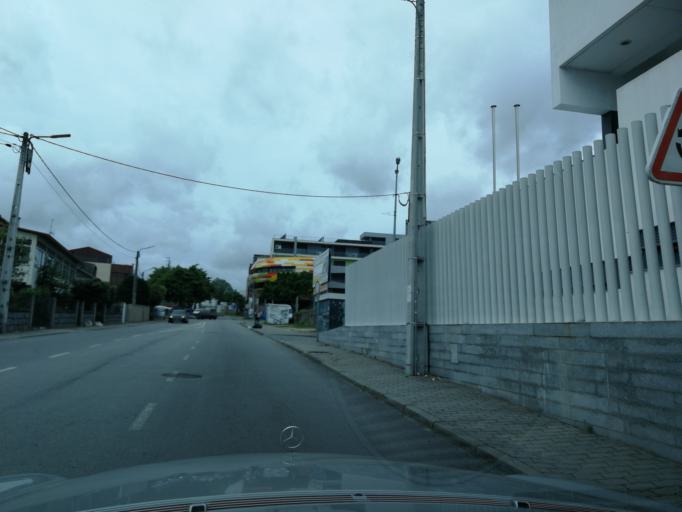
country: PT
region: Braga
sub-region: Amares
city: Amares
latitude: 41.6256
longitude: -8.3609
